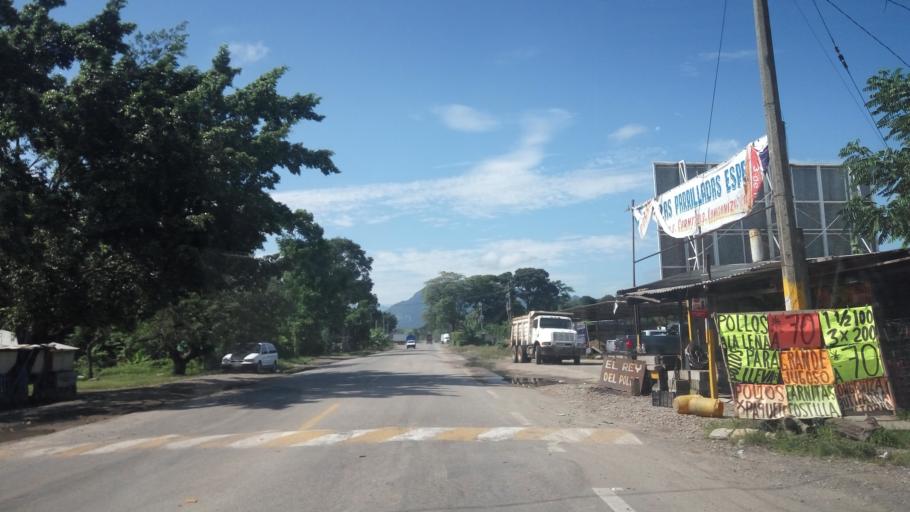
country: MX
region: Tabasco
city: Teapa
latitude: 17.5938
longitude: -92.9646
